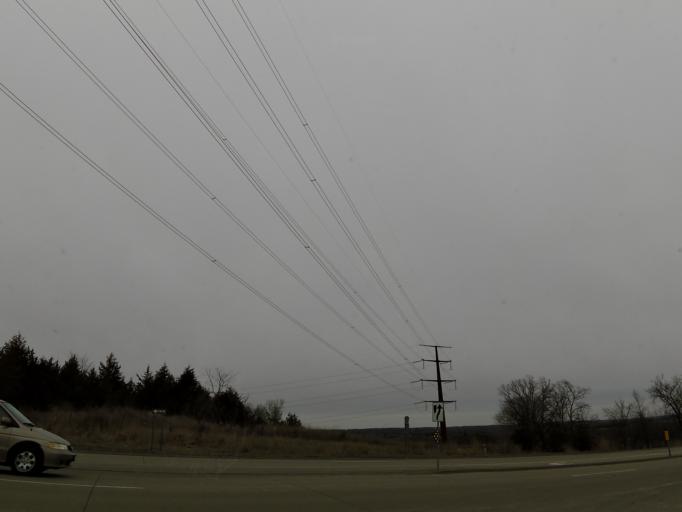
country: US
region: Minnesota
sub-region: Scott County
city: Belle Plaine
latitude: 44.6000
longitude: -93.7985
